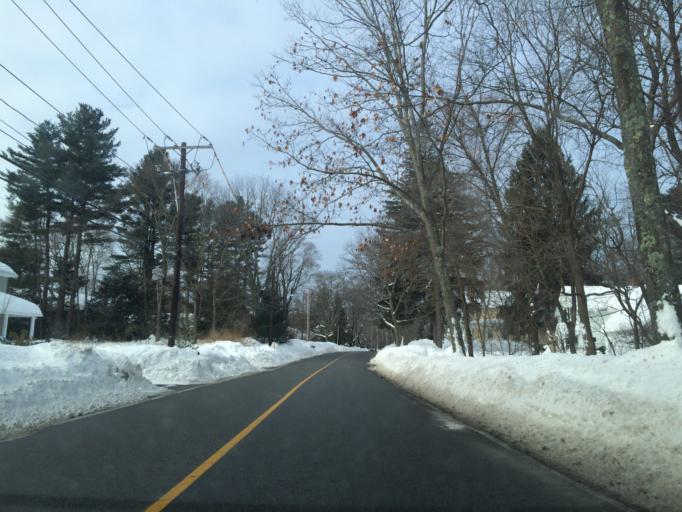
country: US
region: Massachusetts
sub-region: Middlesex County
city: Weston
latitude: 42.3656
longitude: -71.3108
